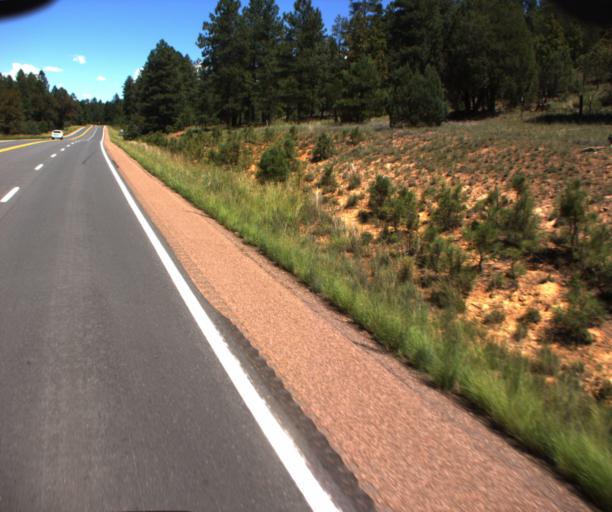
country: US
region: Arizona
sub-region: Navajo County
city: Show Low
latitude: 34.1791
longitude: -110.0959
